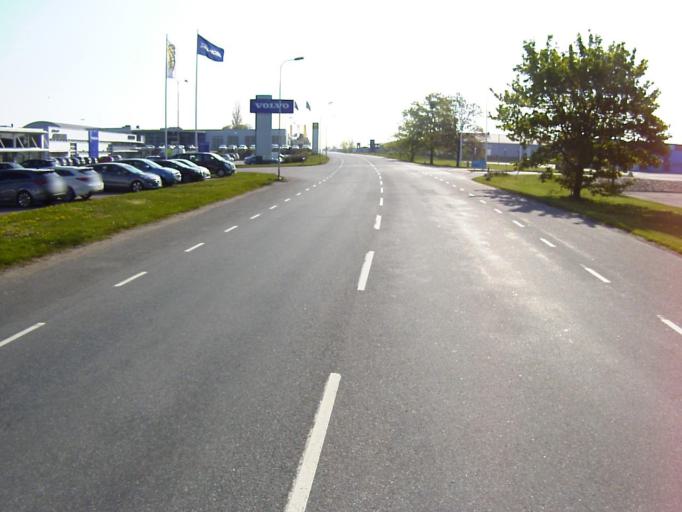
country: SE
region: Skane
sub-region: Kristianstads Kommun
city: Kristianstad
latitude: 56.0281
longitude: 14.2110
